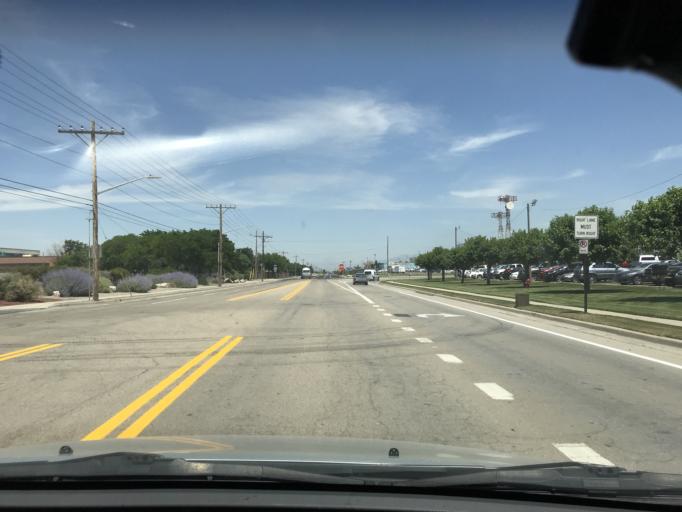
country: US
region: Utah
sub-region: Salt Lake County
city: Salt Lake City
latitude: 40.7837
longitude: -111.9535
